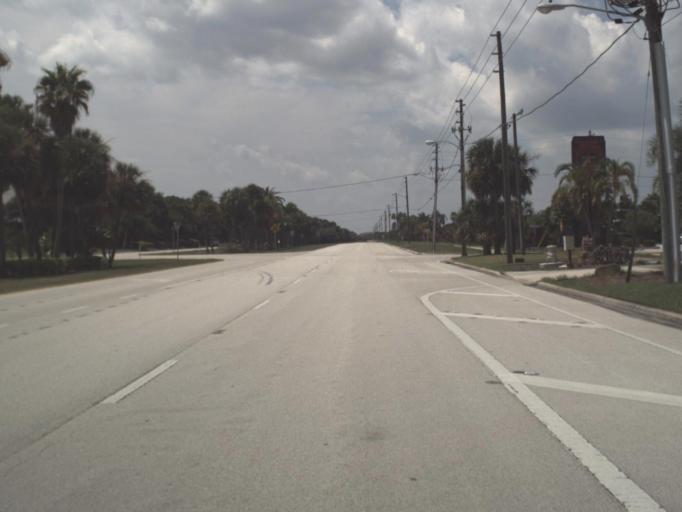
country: US
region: Florida
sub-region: Pinellas County
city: Tierra Verde
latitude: 27.6751
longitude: -82.7260
